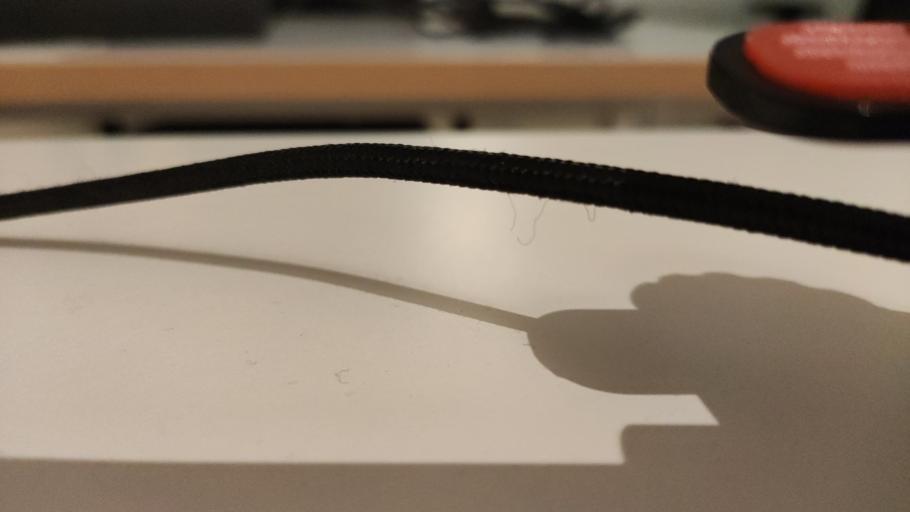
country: RU
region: Moskovskaya
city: Likino-Dulevo
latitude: 55.7136
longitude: 38.9580
